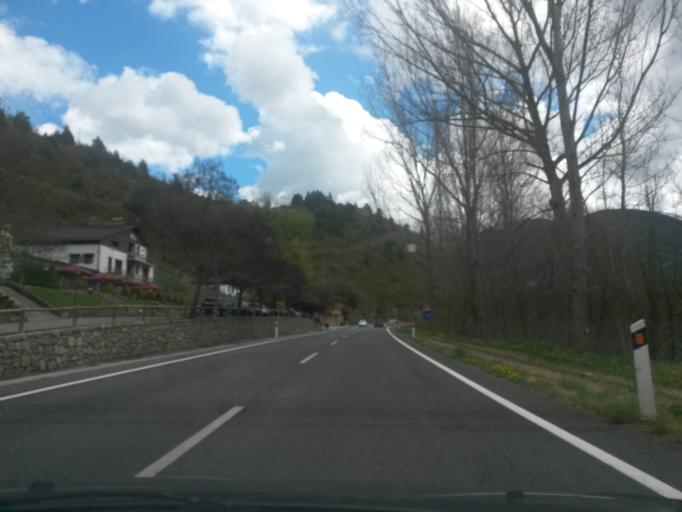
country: ES
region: Catalonia
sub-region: Provincia de Lleida
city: Lles de Cerdanya
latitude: 42.3653
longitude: 1.6799
